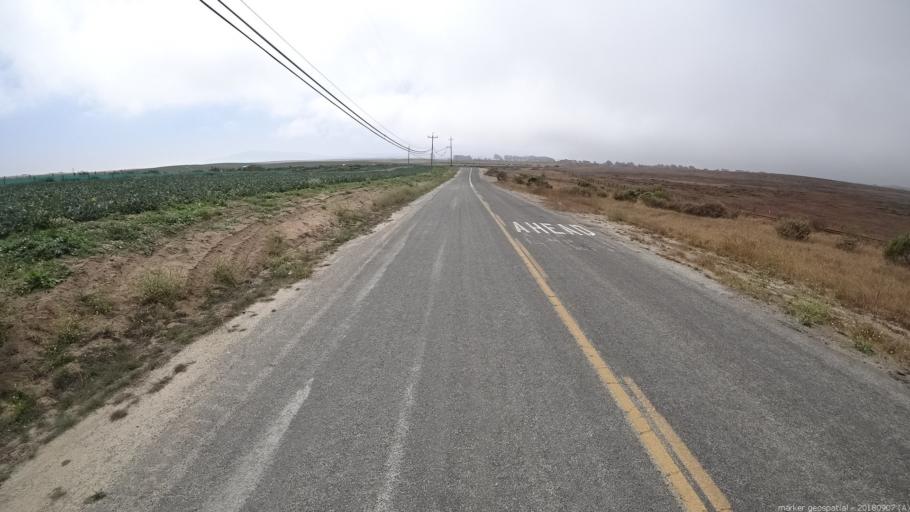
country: US
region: California
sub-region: Monterey County
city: Marina
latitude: 36.7073
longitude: -121.7893
